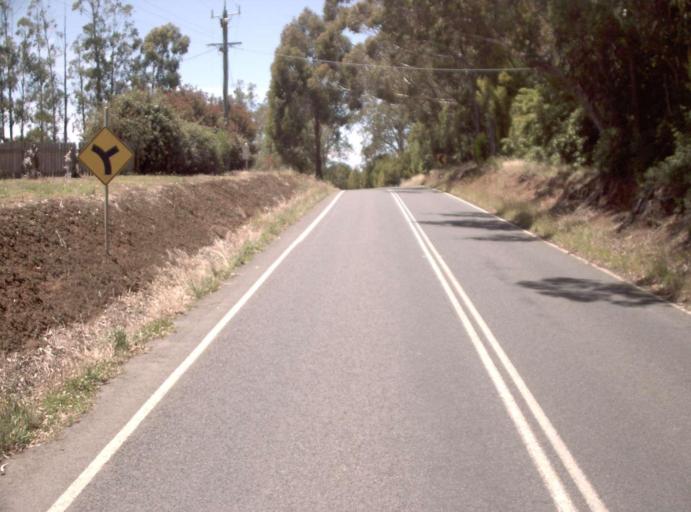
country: AU
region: Victoria
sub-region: Baw Baw
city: Warragul
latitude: -38.0313
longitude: 145.9533
